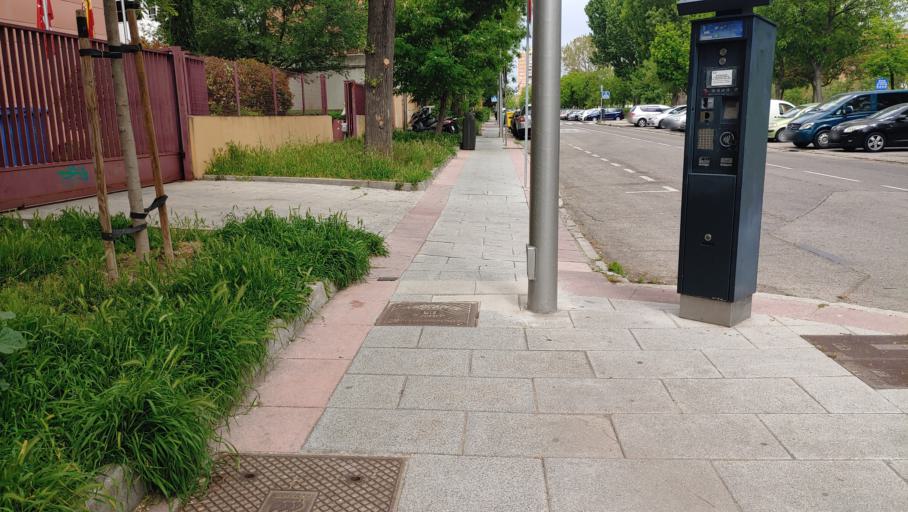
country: ES
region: Madrid
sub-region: Provincia de Madrid
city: Moncloa-Aravaca
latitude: 40.4277
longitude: -3.7312
